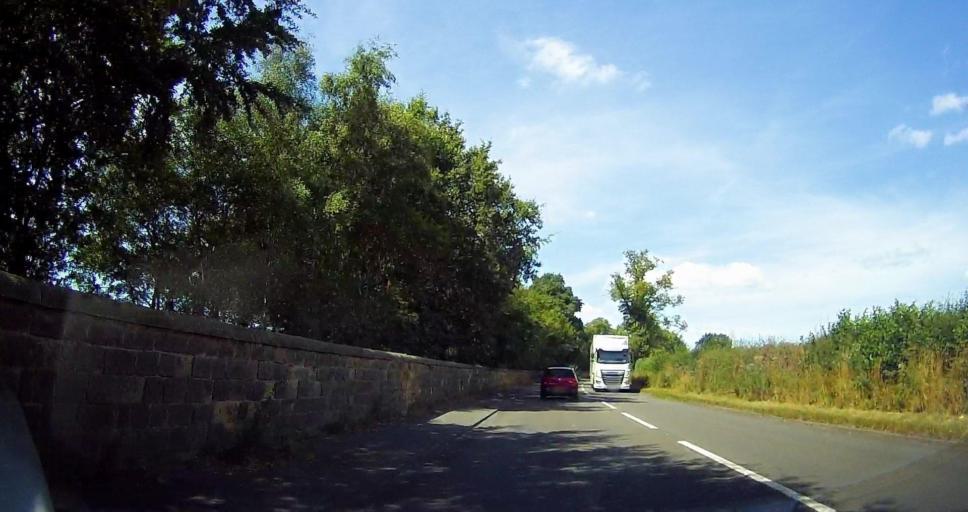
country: GB
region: England
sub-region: Staffordshire
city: Codsall
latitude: 52.6147
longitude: -2.2092
